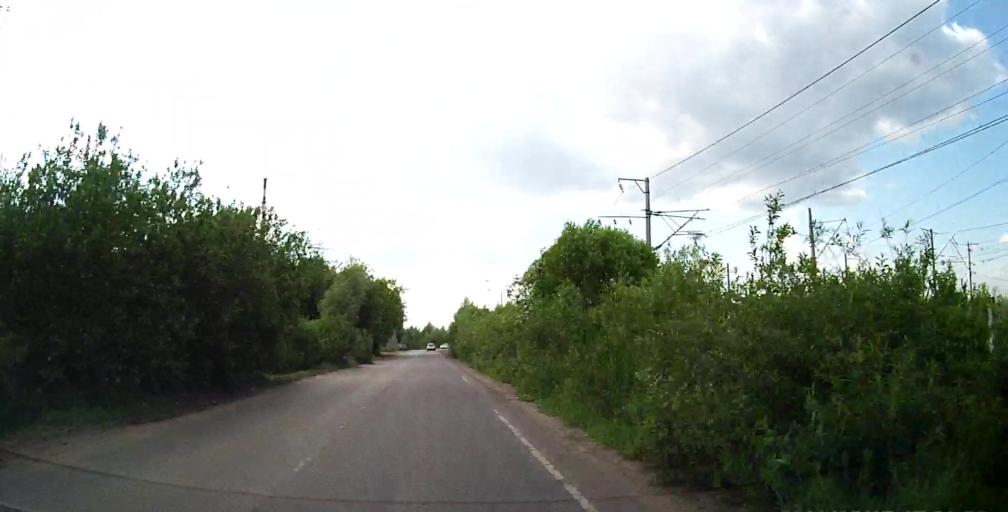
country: RU
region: Moskovskaya
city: Shcherbinka
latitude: 55.5166
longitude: 37.5367
